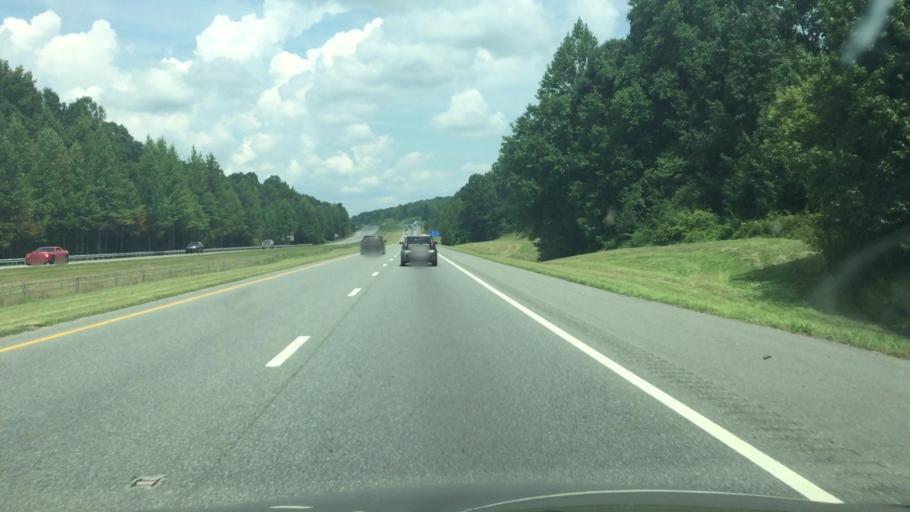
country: US
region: North Carolina
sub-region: Montgomery County
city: Biscoe
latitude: 35.5050
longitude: -79.7811
